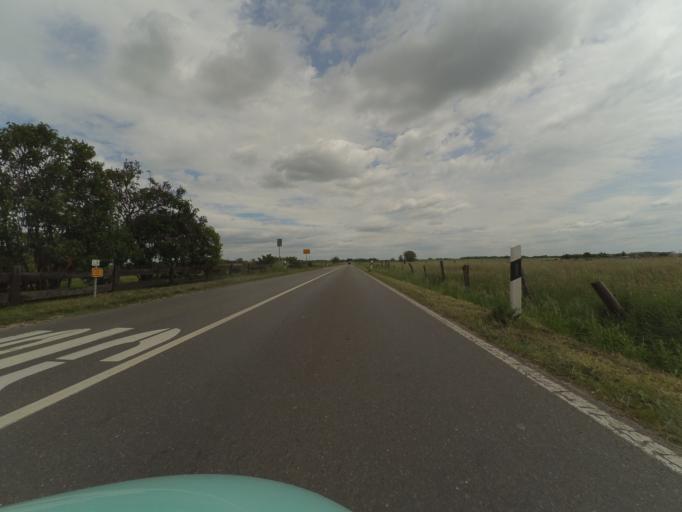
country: DE
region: Lower Saxony
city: Wunstorf
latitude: 52.4430
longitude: 9.4214
